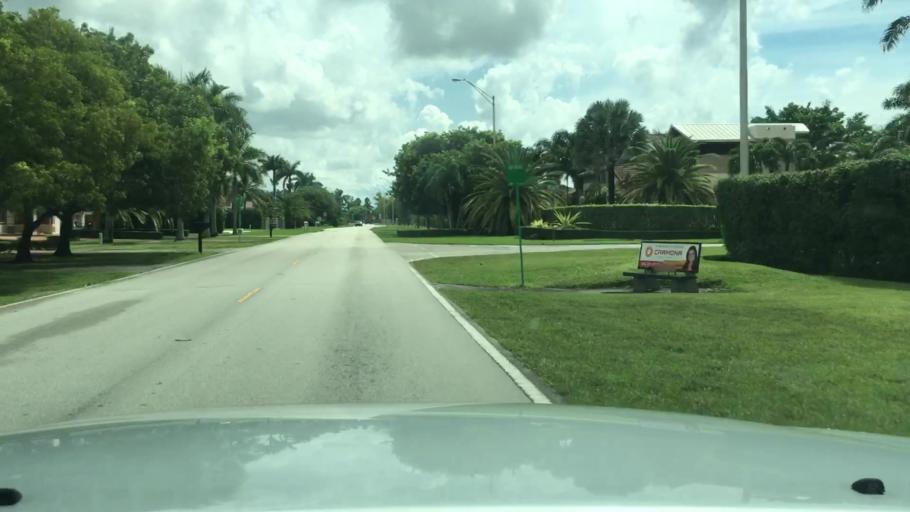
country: US
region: Florida
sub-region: Miami-Dade County
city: Tamiami
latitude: 25.7733
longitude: -80.3975
